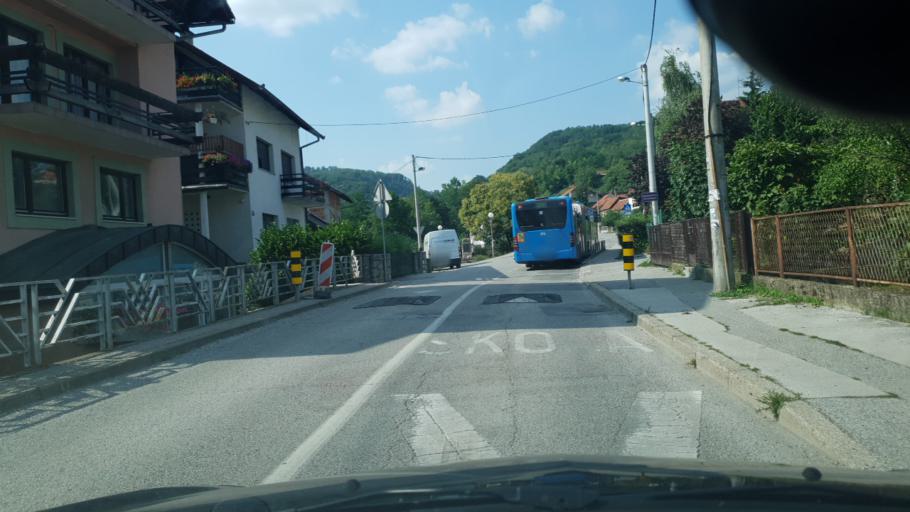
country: HR
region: Grad Zagreb
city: Stenjevec
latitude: 45.8320
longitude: 15.9036
